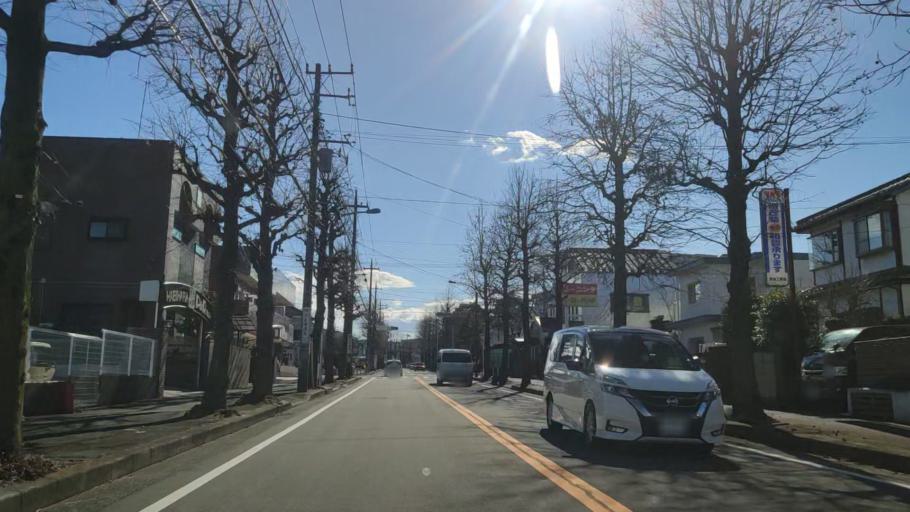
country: JP
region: Tokyo
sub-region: Machida-shi
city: Machida
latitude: 35.5171
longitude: 139.5082
